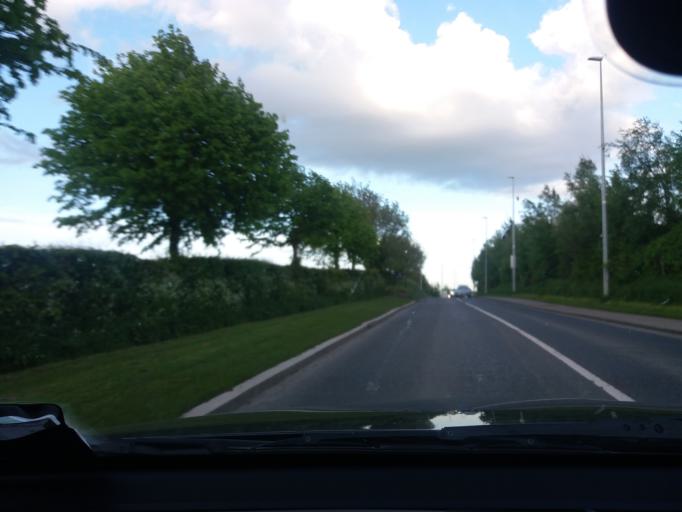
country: IE
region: Leinster
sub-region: South Dublin
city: Rathcoole
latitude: 53.2944
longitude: -6.4849
